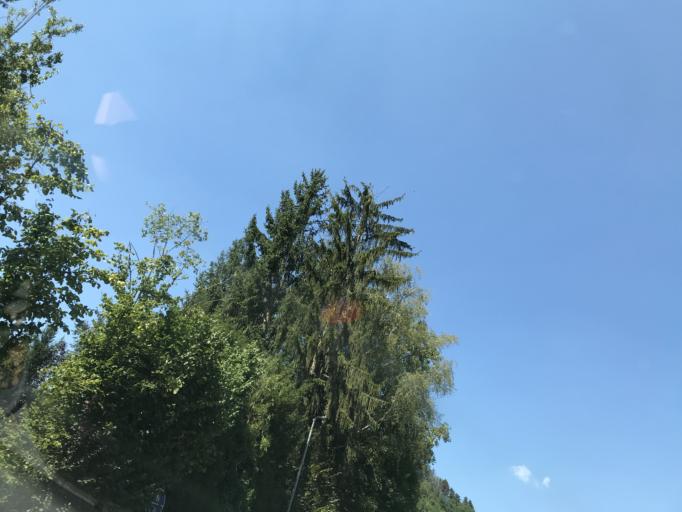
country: DE
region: Baden-Wuerttemberg
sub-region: Freiburg Region
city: Stegen
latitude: 47.9962
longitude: 7.9743
